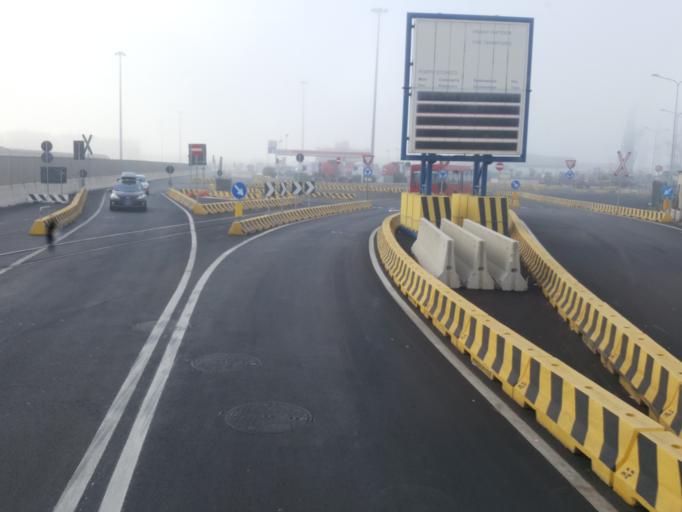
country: IT
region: Latium
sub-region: Citta metropolitana di Roma Capitale
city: Civitavecchia
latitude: 42.1064
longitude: 11.7779
